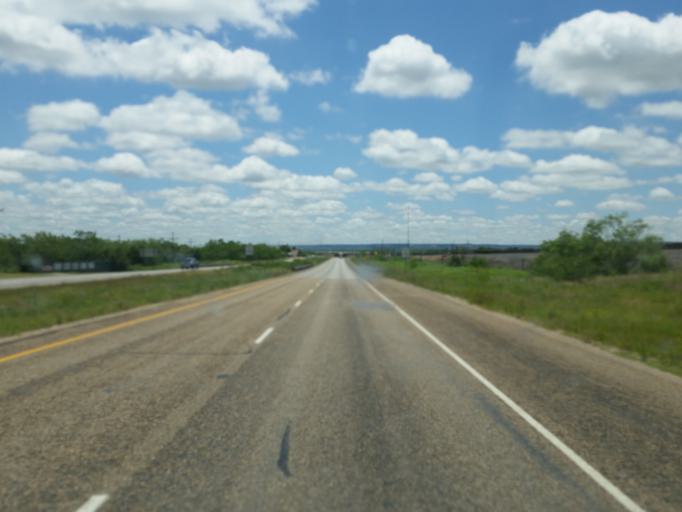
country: US
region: Texas
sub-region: Garza County
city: Post
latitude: 33.0473
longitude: -101.2066
